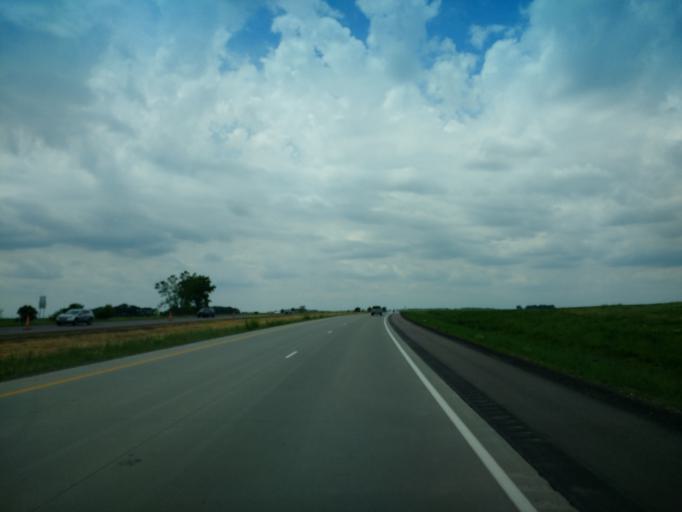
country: US
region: Minnesota
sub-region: Cottonwood County
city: Mountain Lake
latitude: 43.9287
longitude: -94.9629
